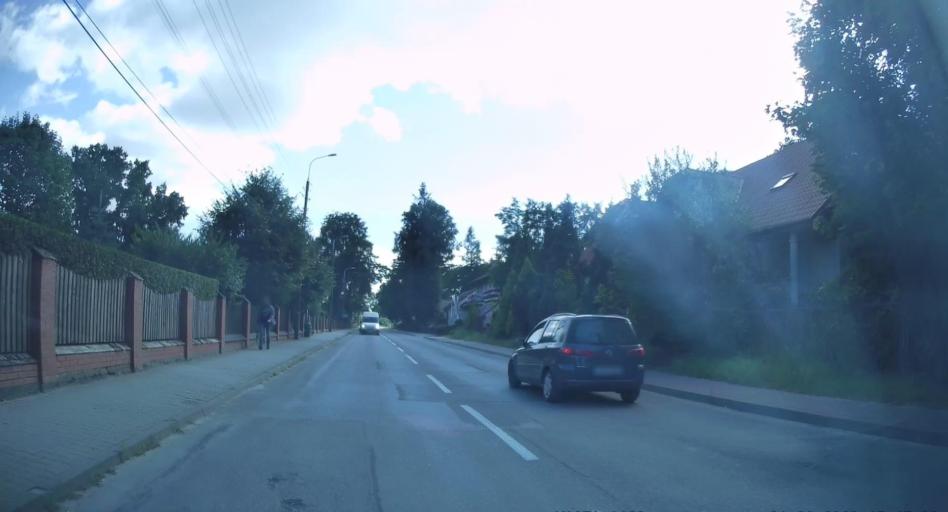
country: PL
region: Swietokrzyskie
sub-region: Powiat skarzyski
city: Suchedniow
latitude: 51.0465
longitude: 20.8385
